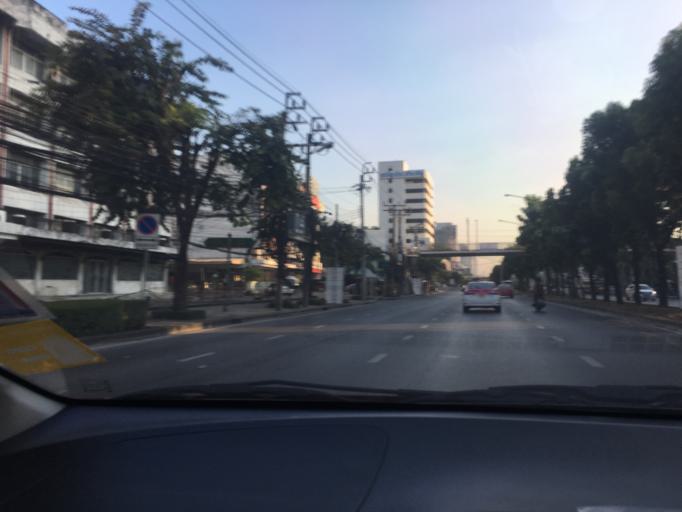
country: TH
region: Bangkok
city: Huai Khwang
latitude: 13.7979
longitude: 100.5746
